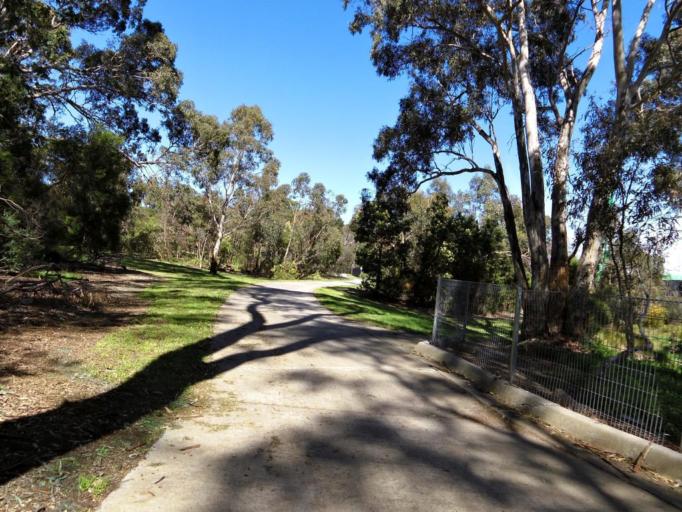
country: AU
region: Victoria
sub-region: Greater Dandenong
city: Dandenong
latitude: -37.9732
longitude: 145.1948
